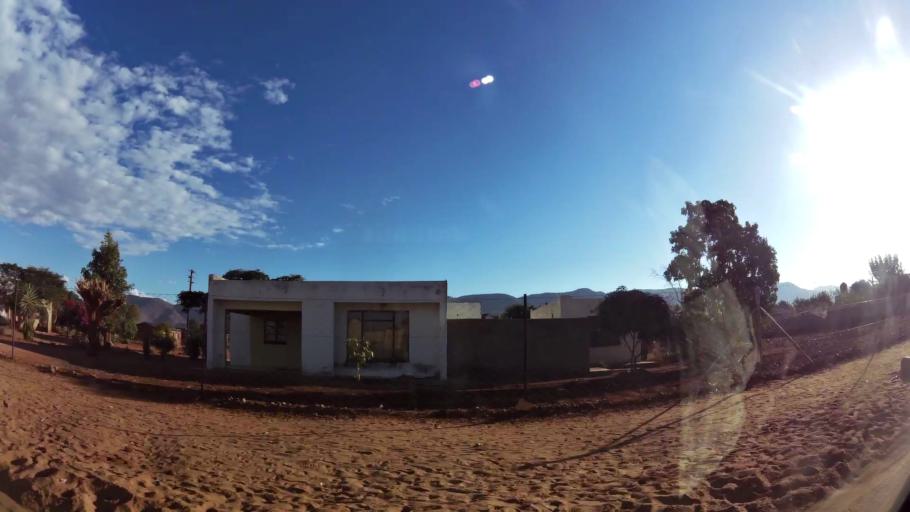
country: ZA
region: Limpopo
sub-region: Waterberg District Municipality
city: Mokopane
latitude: -24.1703
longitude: 28.9753
